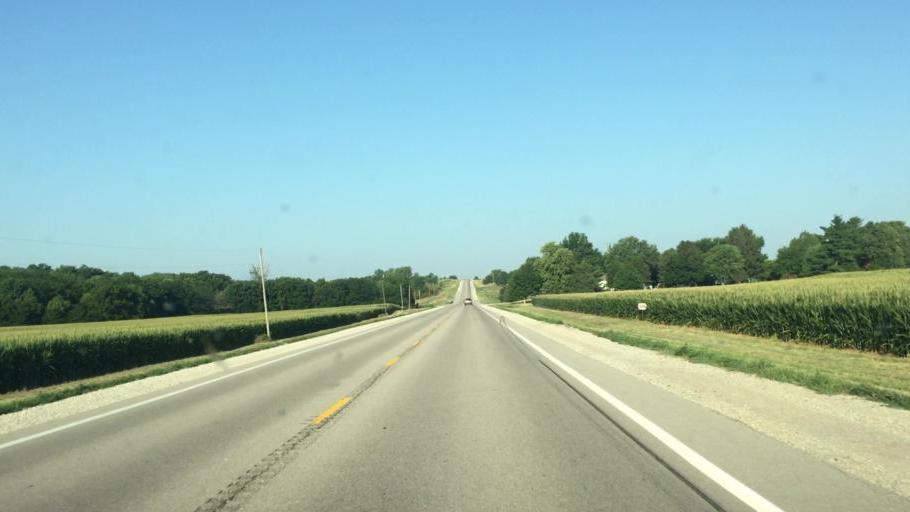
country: US
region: Kansas
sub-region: Nemaha County
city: Sabetha
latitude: 39.8457
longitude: -95.6785
